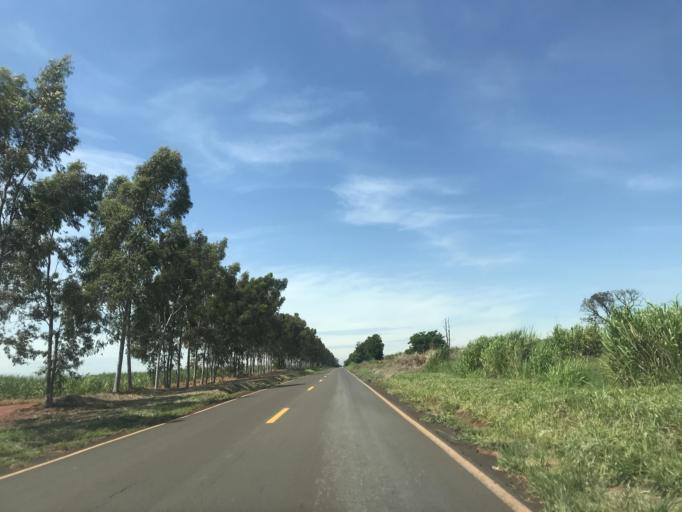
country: BR
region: Parana
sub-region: Paranavai
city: Nova Aurora
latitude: -22.8301
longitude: -52.6559
